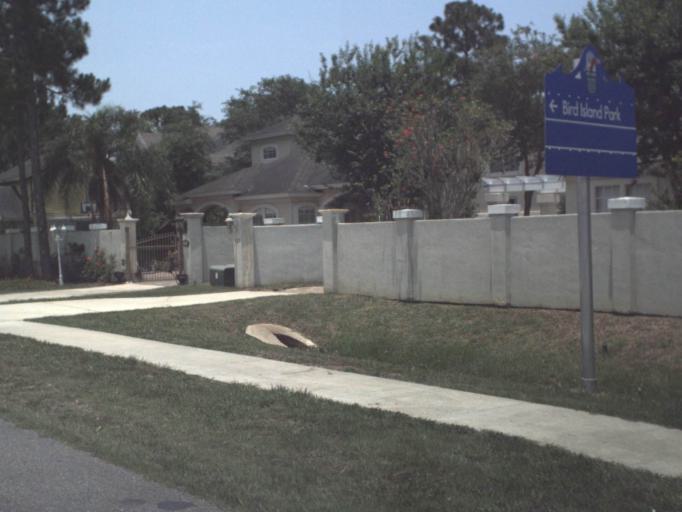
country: US
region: Florida
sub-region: Saint Johns County
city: Ponte Vedra Beach
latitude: 30.2248
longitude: -81.3844
